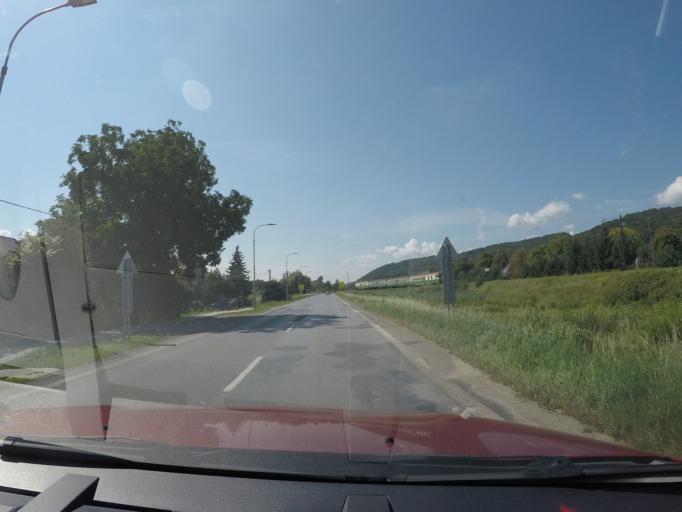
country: SK
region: Presovsky
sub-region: Okres Presov
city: Presov
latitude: 48.9570
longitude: 21.2414
